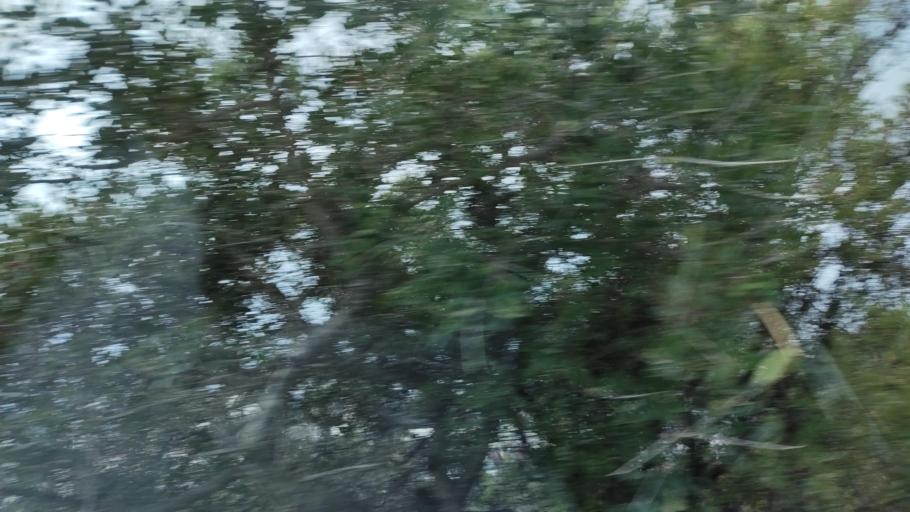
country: GI
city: Gibraltar
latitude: 36.1240
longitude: -5.3465
